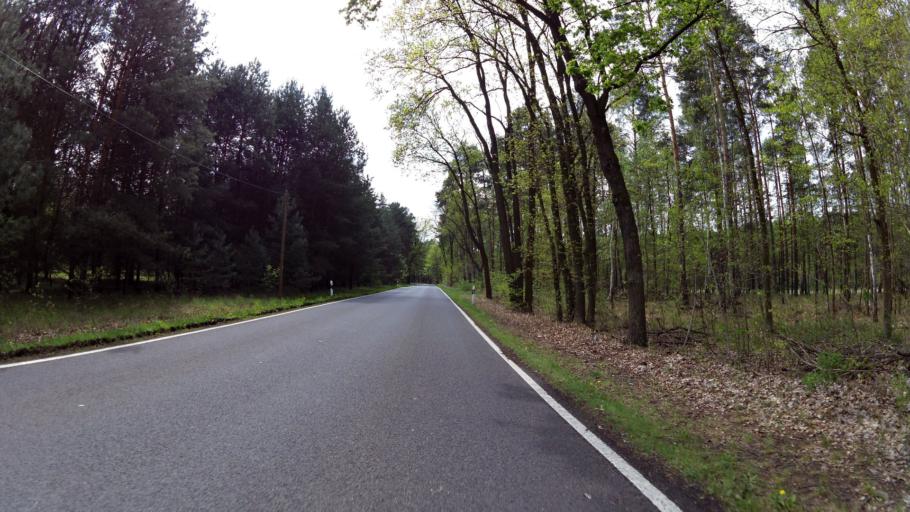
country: DE
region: Brandenburg
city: Bestensee
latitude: 52.2803
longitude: 13.7348
